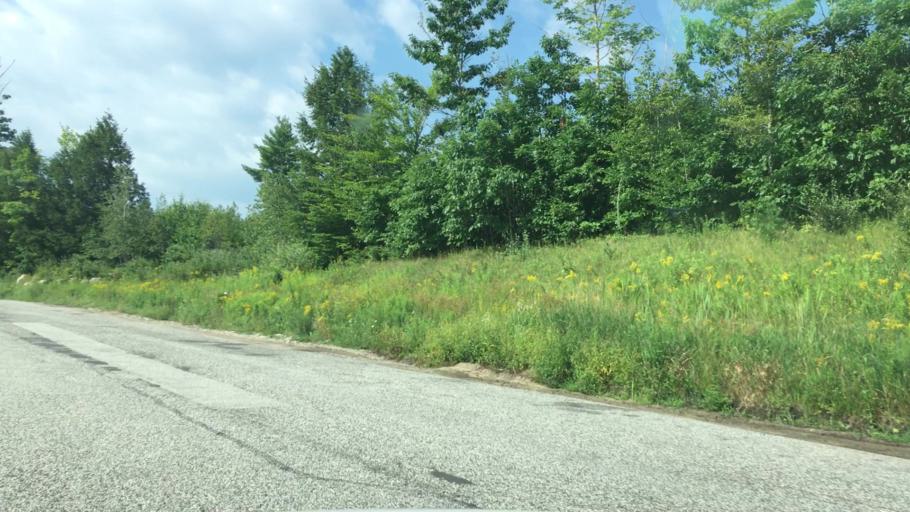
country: US
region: Maine
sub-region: Cumberland County
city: New Gloucester
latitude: 44.0323
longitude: -70.2704
